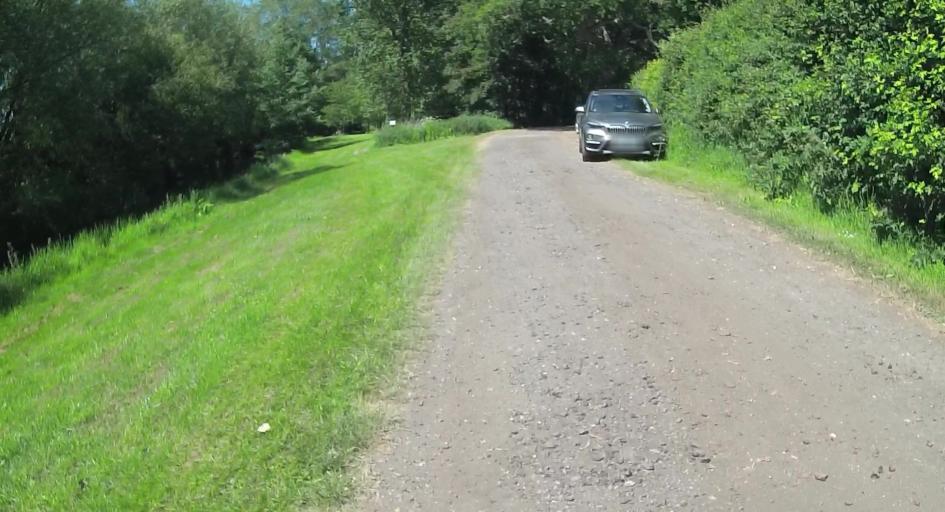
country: GB
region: England
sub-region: West Berkshire
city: Stratfield Mortimer
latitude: 51.3415
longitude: -1.0086
